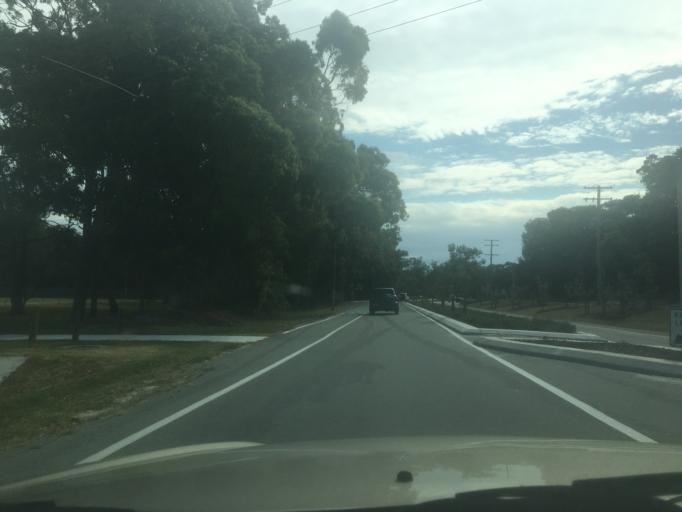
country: AU
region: Queensland
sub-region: Moreton Bay
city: Bongaree
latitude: -27.0812
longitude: 153.1727
